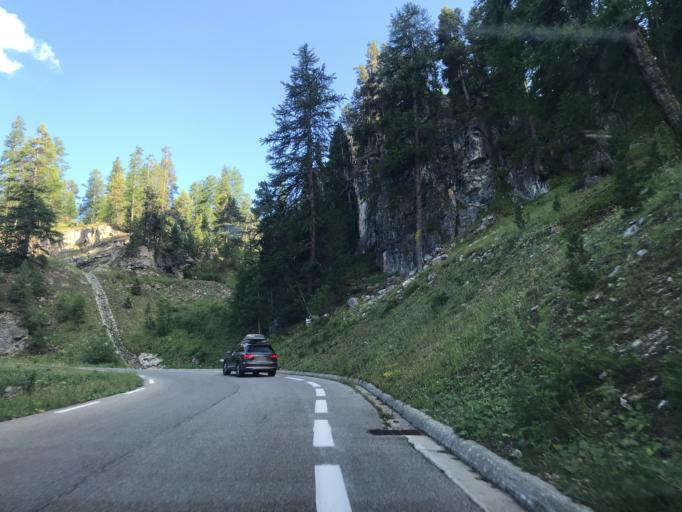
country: FR
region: Provence-Alpes-Cote d'Azur
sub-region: Departement des Hautes-Alpes
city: Villar-Saint-Pancrace
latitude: 44.8325
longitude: 6.7226
